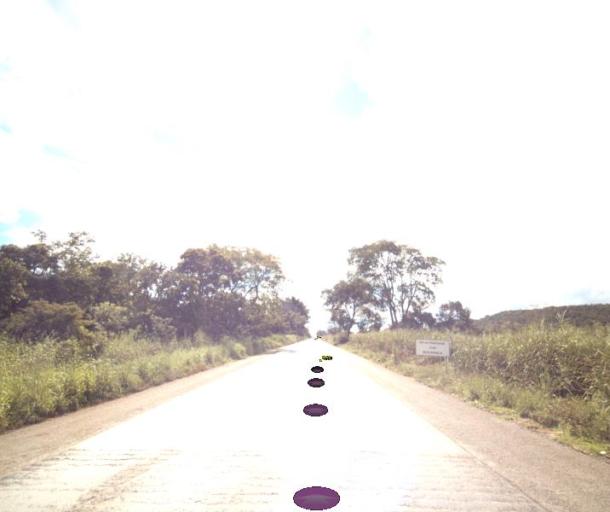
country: BR
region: Goias
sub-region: Petrolina De Goias
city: Petrolina de Goias
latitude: -15.9289
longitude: -49.2093
